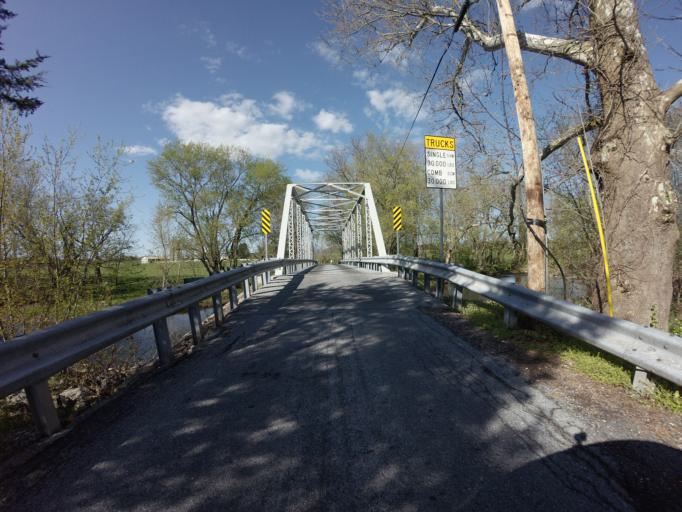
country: US
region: Maryland
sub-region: Frederick County
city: Emmitsburg
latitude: 39.6481
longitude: -77.2891
